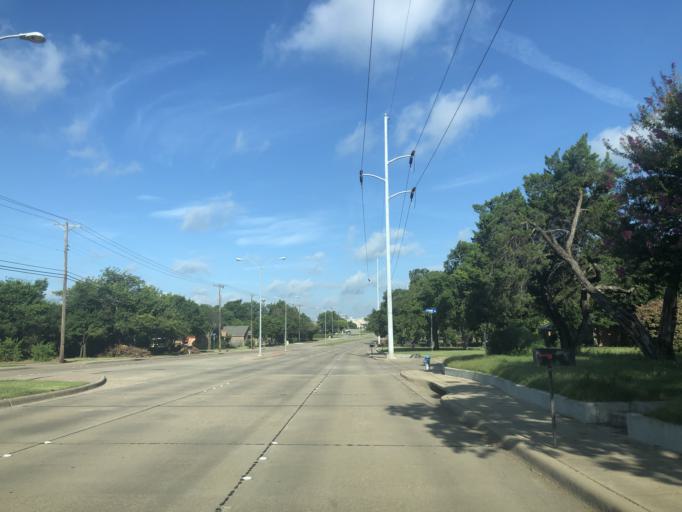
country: US
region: Texas
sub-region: Dallas County
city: Duncanville
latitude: 32.6618
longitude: -96.9209
